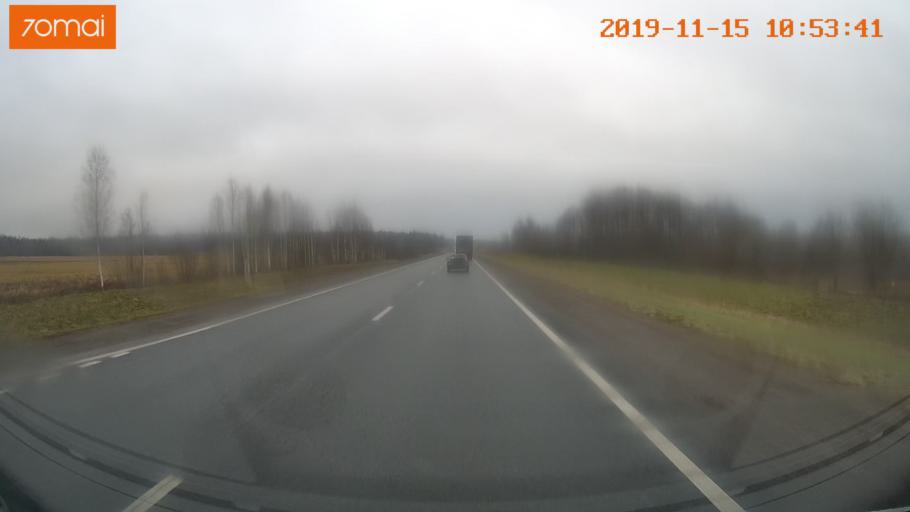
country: RU
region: Vologda
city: Chebsara
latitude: 59.1679
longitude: 38.7598
